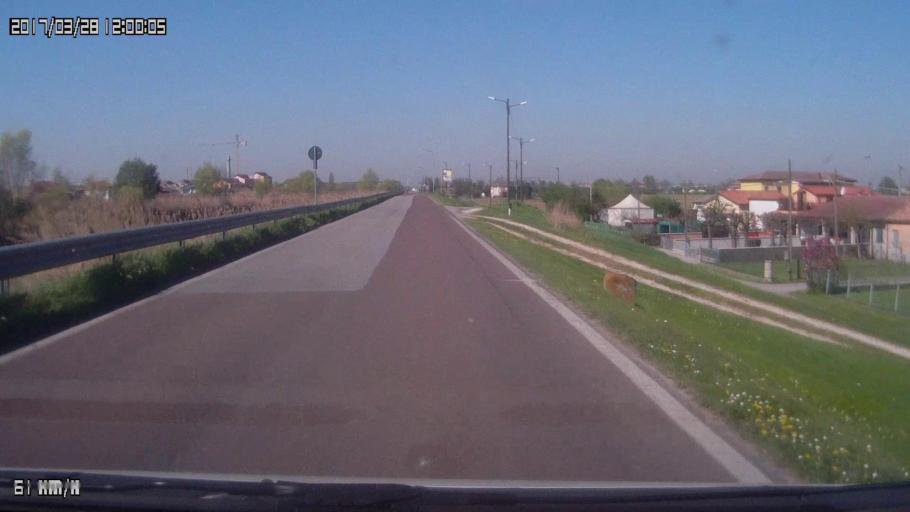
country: IT
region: Veneto
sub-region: Provincia di Venezia
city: Cavarzere
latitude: 45.1429
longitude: 12.0964
